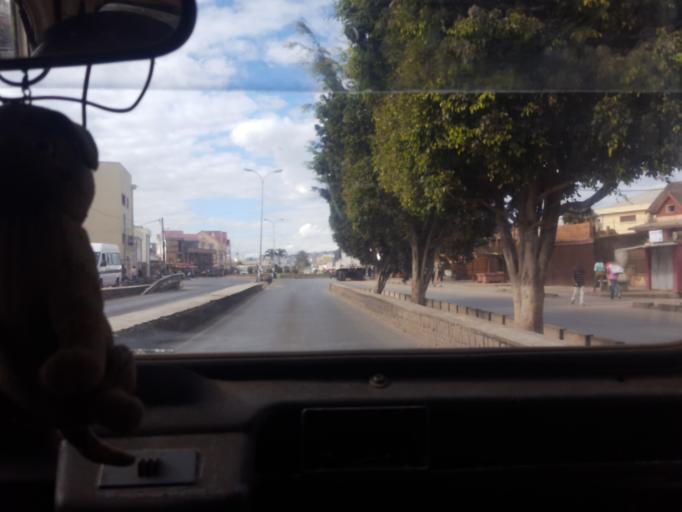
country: MG
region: Analamanga
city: Antananarivo
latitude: -18.9339
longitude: 47.5051
